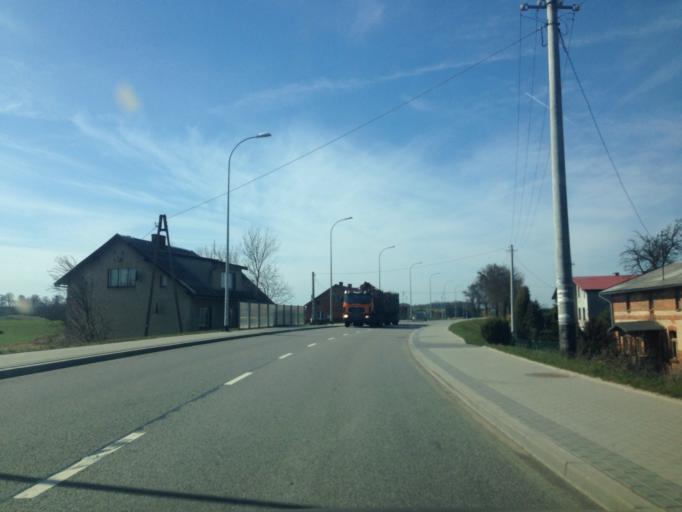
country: PL
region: Pomeranian Voivodeship
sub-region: Powiat starogardzki
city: Smetowo Graniczne
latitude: 53.7331
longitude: 18.7285
